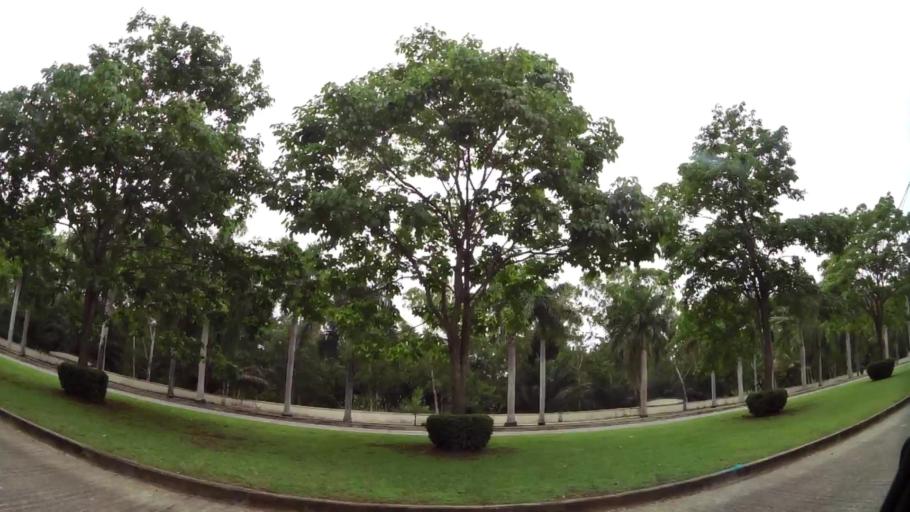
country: PA
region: Panama
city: San Miguelito
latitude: 9.0108
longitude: -79.4595
